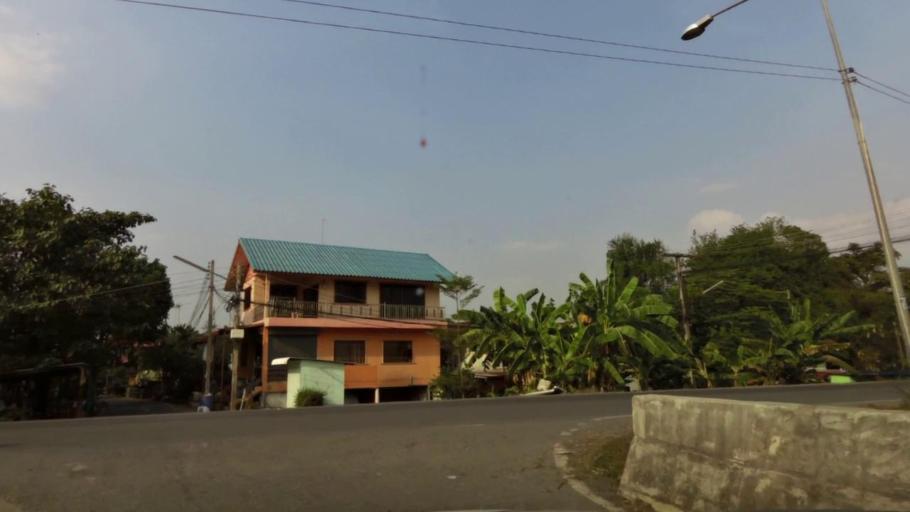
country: TH
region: Phra Nakhon Si Ayutthaya
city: Phra Nakhon Si Ayutthaya
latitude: 14.3334
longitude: 100.5655
